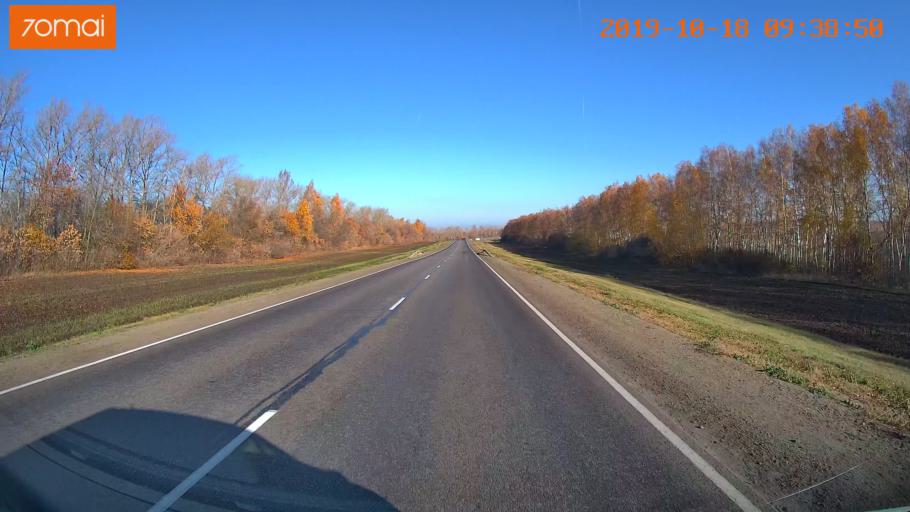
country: RU
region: Tula
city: Yefremov
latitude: 53.2441
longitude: 38.1355
